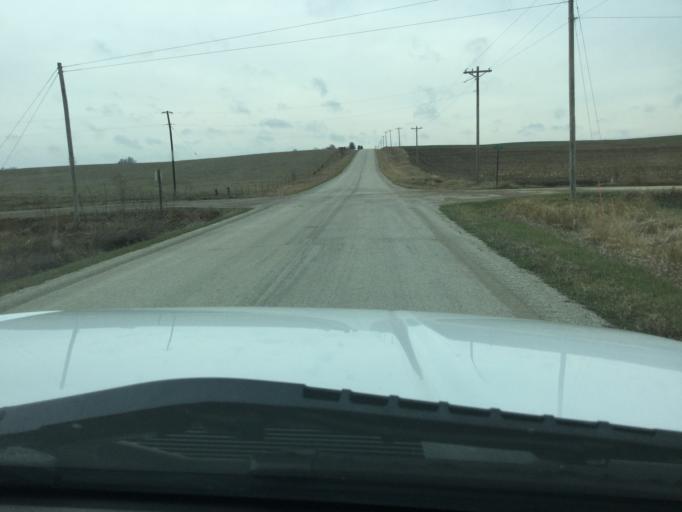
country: US
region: Kansas
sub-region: Nemaha County
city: Sabetha
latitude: 39.8553
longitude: -95.7142
